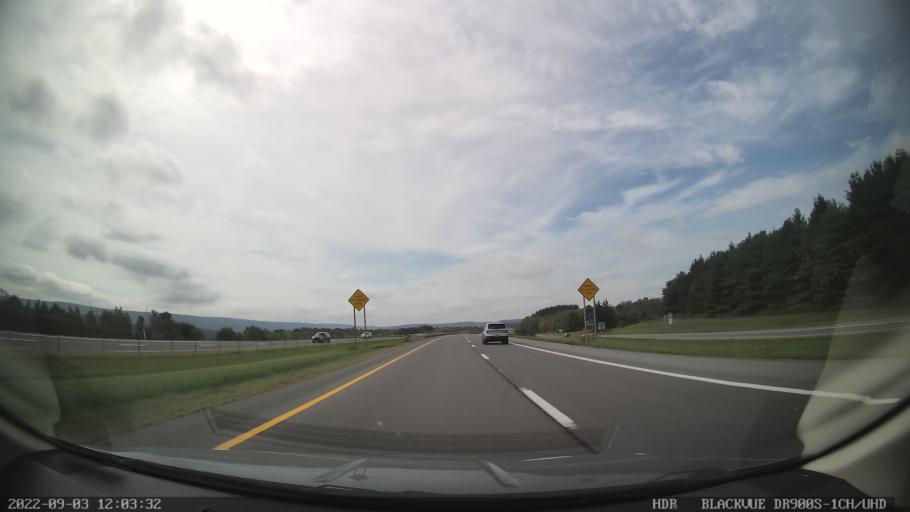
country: US
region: Pennsylvania
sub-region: Tioga County
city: Blossburg
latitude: 41.5618
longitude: -77.1140
